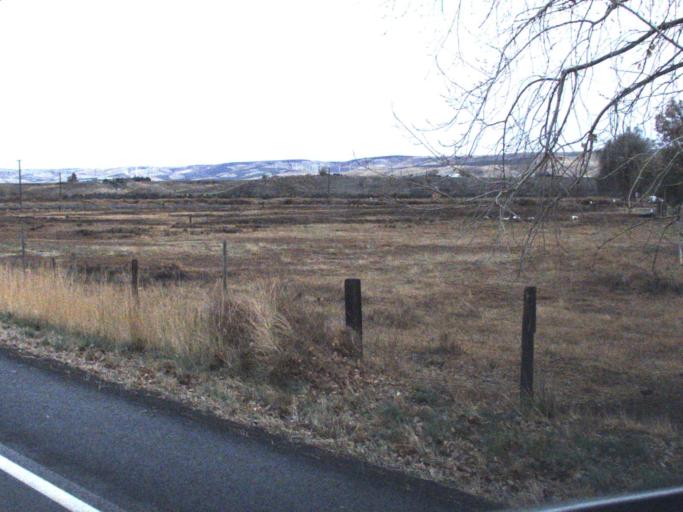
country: US
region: Washington
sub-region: Walla Walla County
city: Garrett
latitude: 46.0433
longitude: -118.6909
